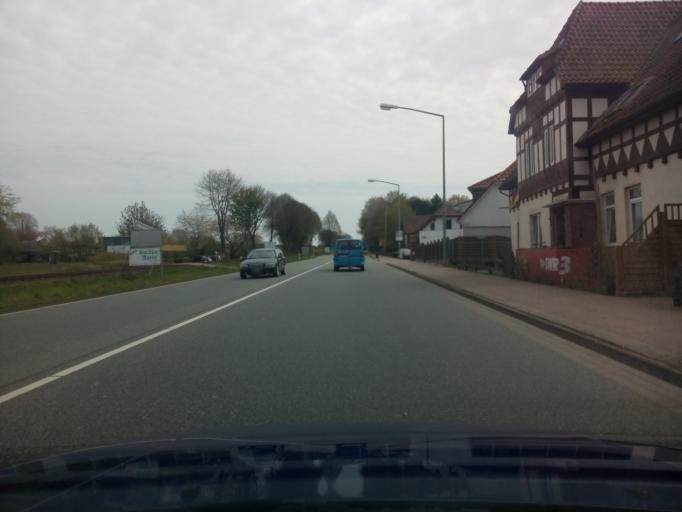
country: DE
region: Lower Saxony
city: Syke
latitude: 52.9083
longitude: 8.8340
